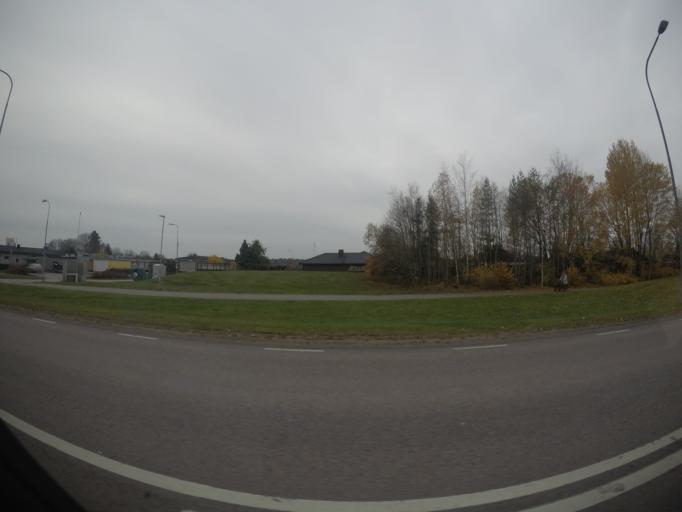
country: SE
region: Vaestmanland
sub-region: Vasteras
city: Vasteras
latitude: 59.6292
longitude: 16.5004
